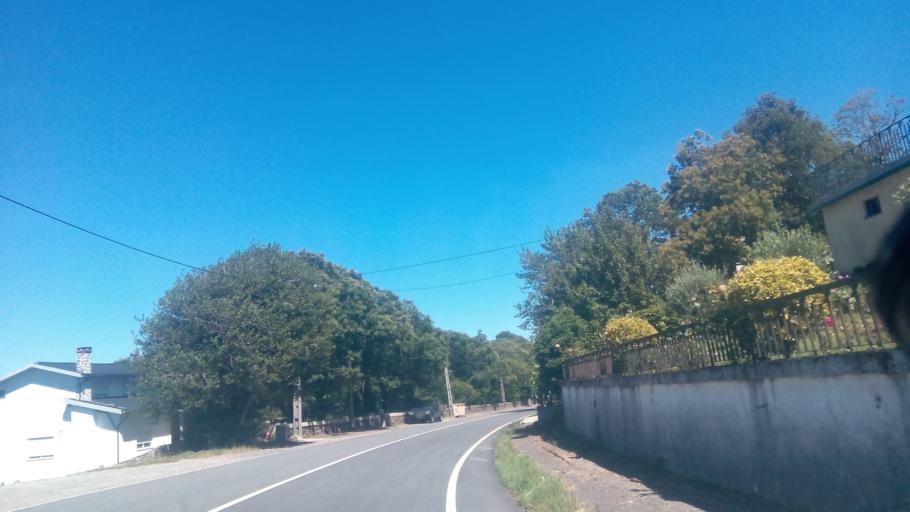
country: PT
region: Vila Real
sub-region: Santa Marta de Penaguiao
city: Santa Marta de Penaguiao
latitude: 41.2807
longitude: -7.8647
